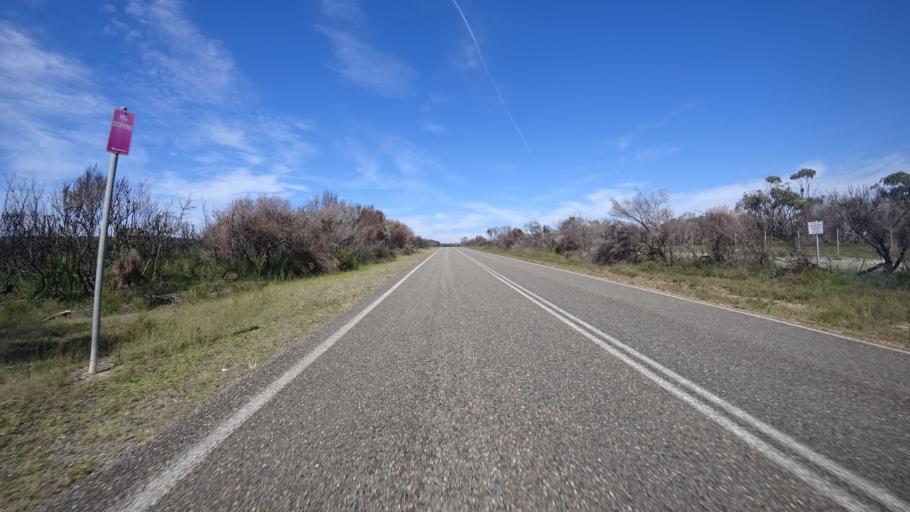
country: AU
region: New South Wales
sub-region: Shoalhaven Shire
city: Falls Creek
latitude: -35.1476
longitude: 150.7080
